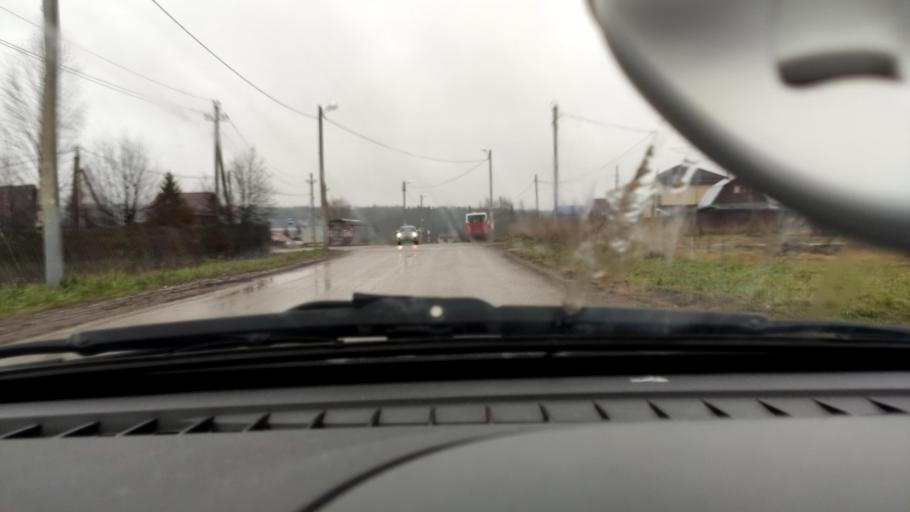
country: RU
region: Perm
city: Perm
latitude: 58.0396
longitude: 56.4082
